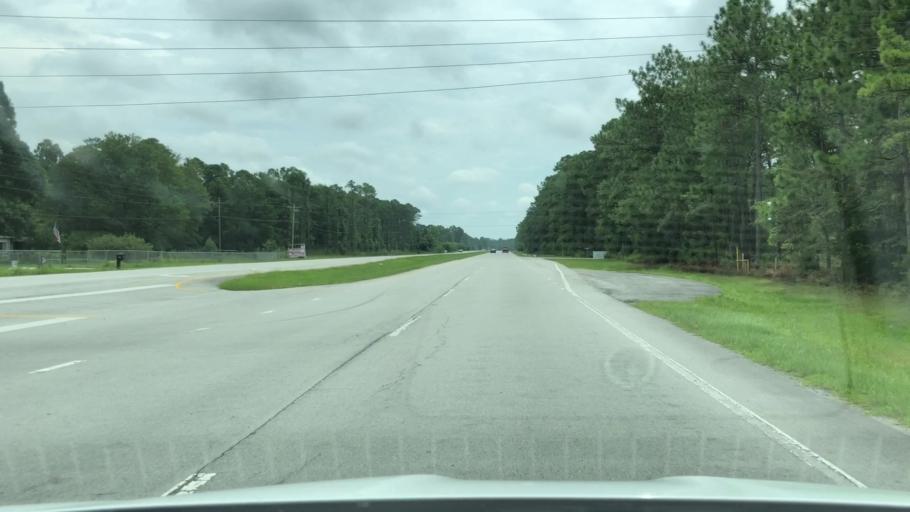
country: US
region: North Carolina
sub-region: Craven County
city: Havelock
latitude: 34.8359
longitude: -76.8820
